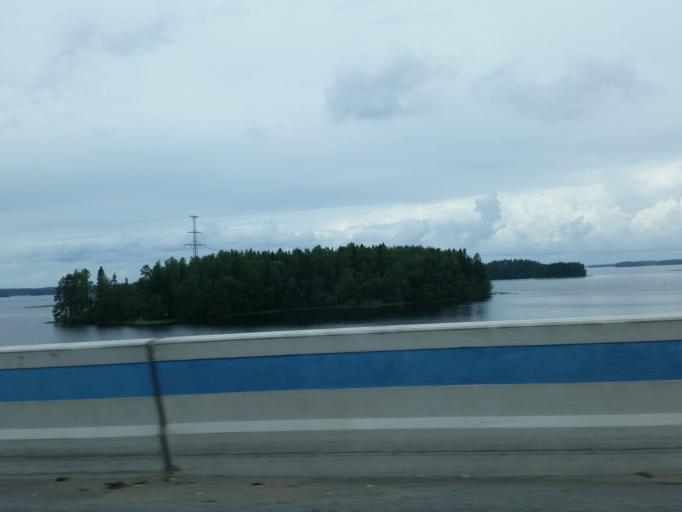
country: FI
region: Northern Savo
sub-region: Kuopio
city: Kuopio
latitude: 62.9466
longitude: 27.6708
